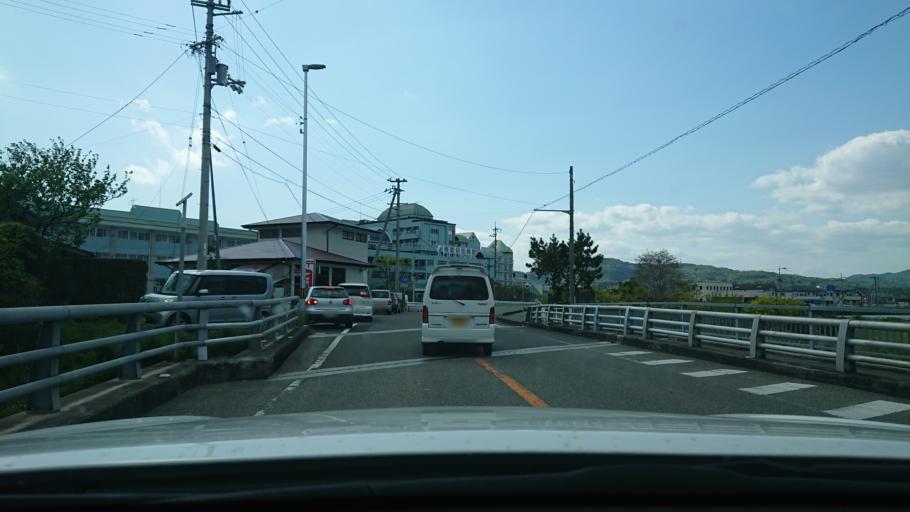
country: JP
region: Tokushima
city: Komatsushimacho
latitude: 34.0212
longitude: 134.5528
